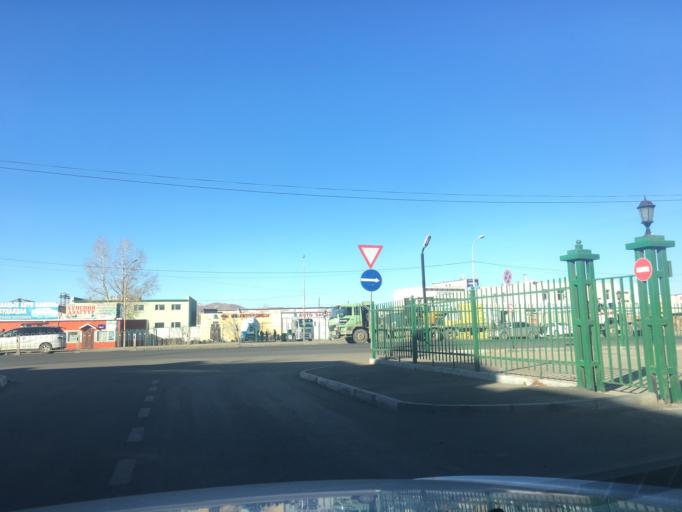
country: MN
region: Ulaanbaatar
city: Ulaanbaatar
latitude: 47.9077
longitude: 106.7946
